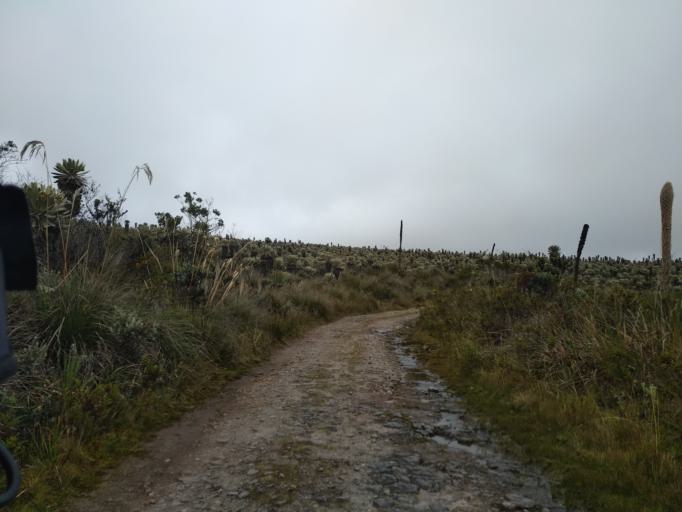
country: EC
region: Carchi
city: San Gabriel
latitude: 0.6861
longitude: -77.8548
